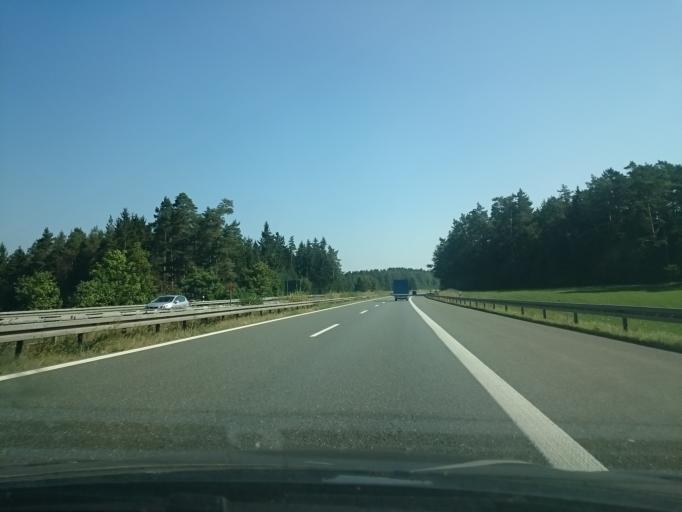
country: DE
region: Bavaria
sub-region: Upper Franconia
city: Stadelhofen
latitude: 50.0064
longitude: 11.2244
